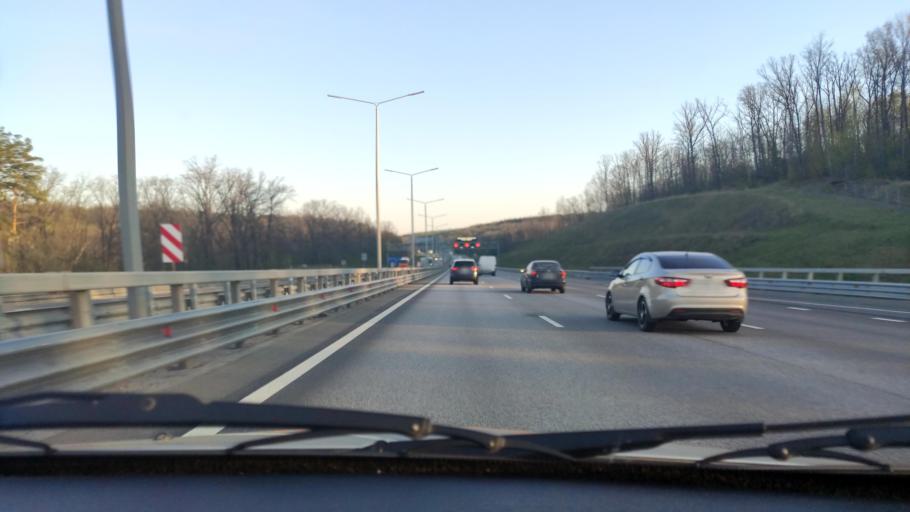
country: RU
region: Voronezj
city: Podgornoye
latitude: 51.8076
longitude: 39.2533
